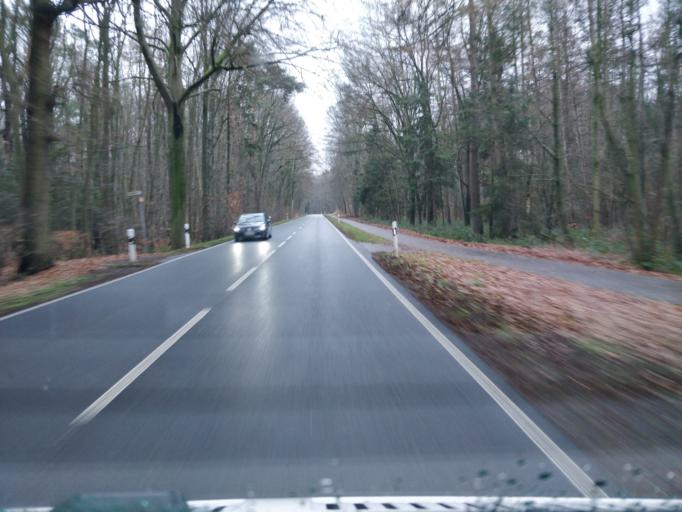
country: DE
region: North Rhine-Westphalia
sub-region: Regierungsbezirk Dusseldorf
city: Mehrhoog
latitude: 51.7672
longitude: 6.4800
